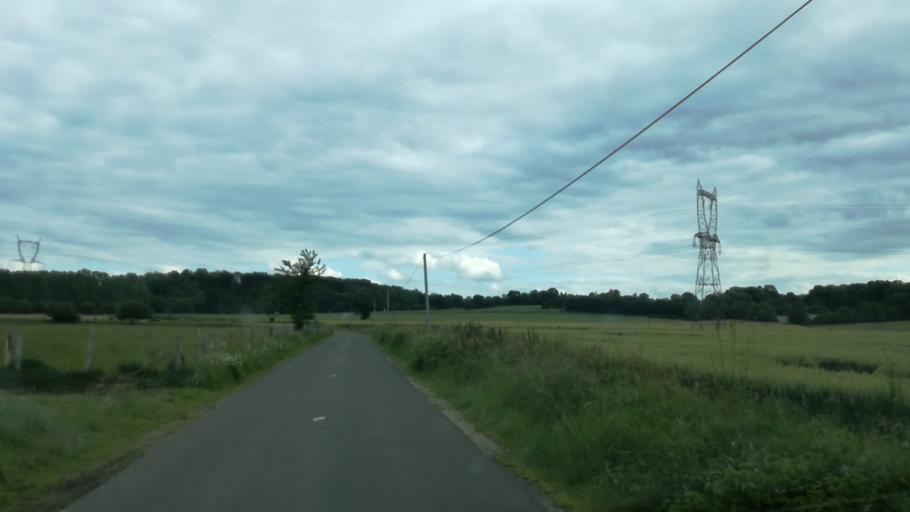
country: FR
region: Haute-Normandie
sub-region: Departement de l'Eure
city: Bourgtheroulde-Infreville
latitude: 49.2737
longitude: 0.8133
